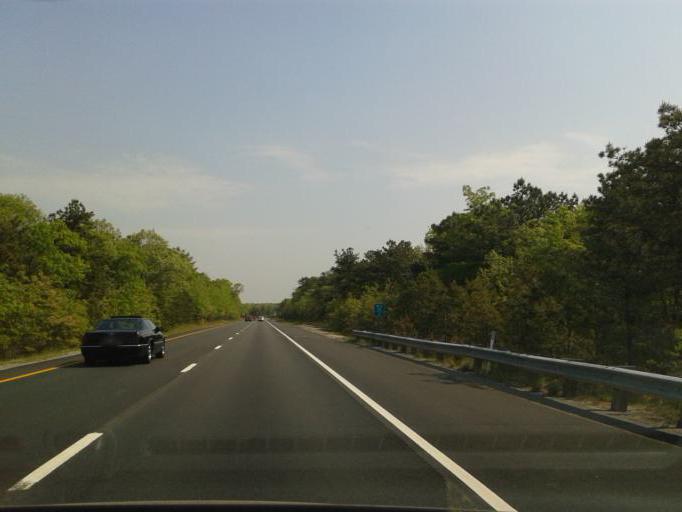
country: US
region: Massachusetts
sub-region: Barnstable County
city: Pocasset
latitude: 41.6797
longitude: -70.5942
